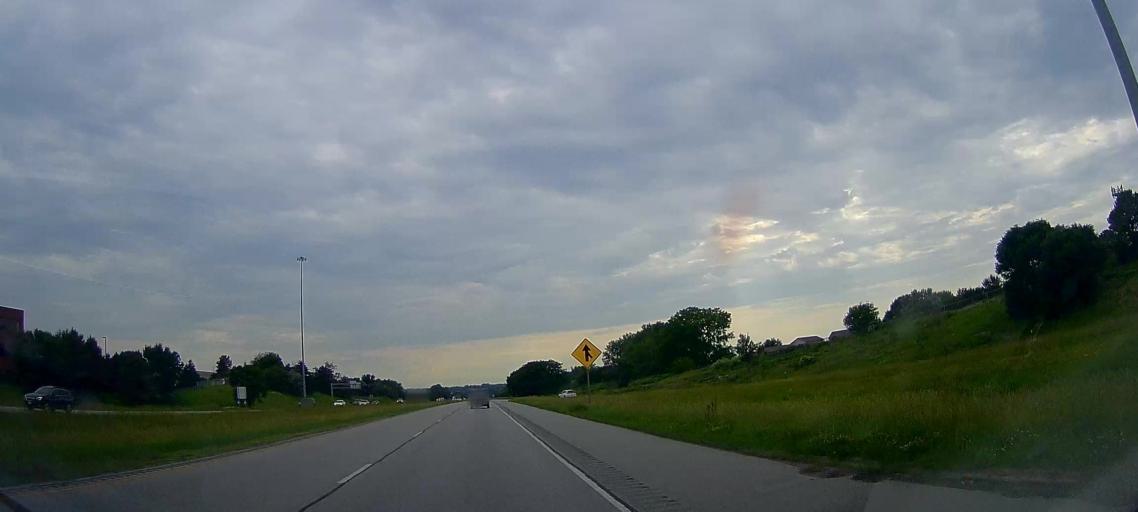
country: US
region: Iowa
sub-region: Pottawattamie County
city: Carter Lake
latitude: 41.3404
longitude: -96.0273
